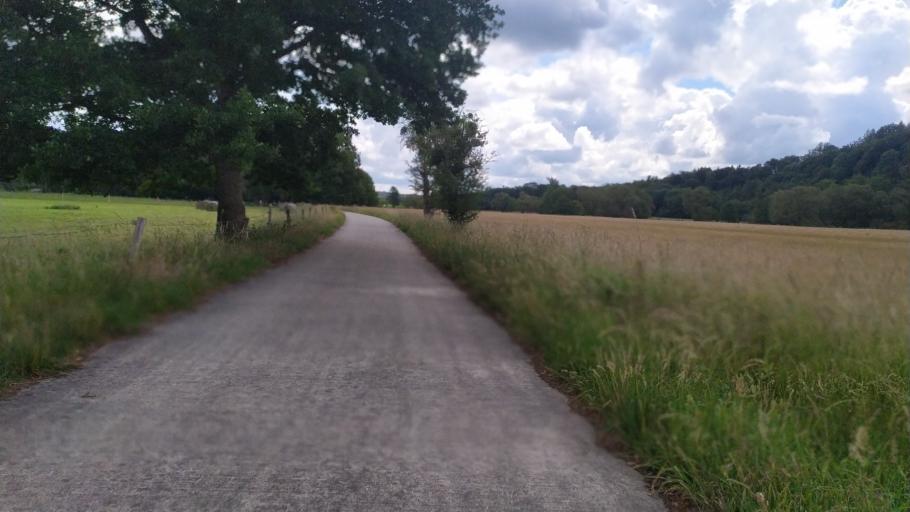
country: BE
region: Wallonia
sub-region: Province de Namur
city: Houyet
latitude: 50.1644
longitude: 5.0884
